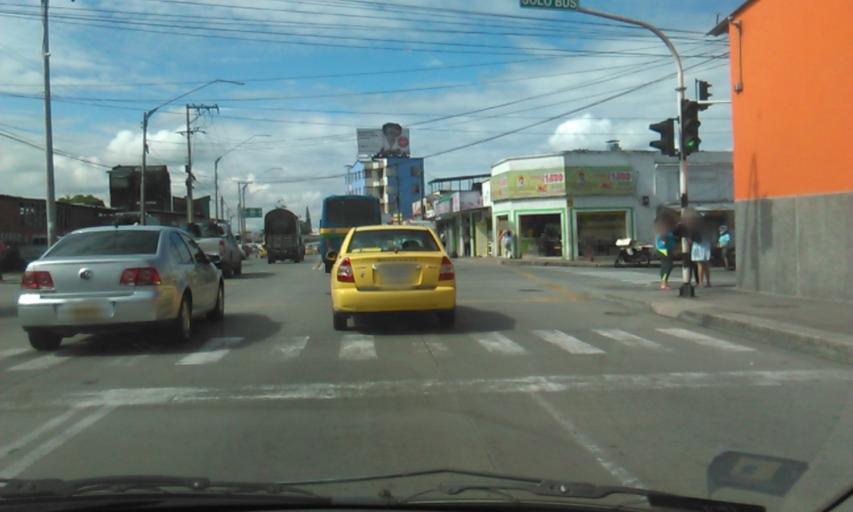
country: CO
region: Quindio
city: Armenia
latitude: 4.5310
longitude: -75.6803
